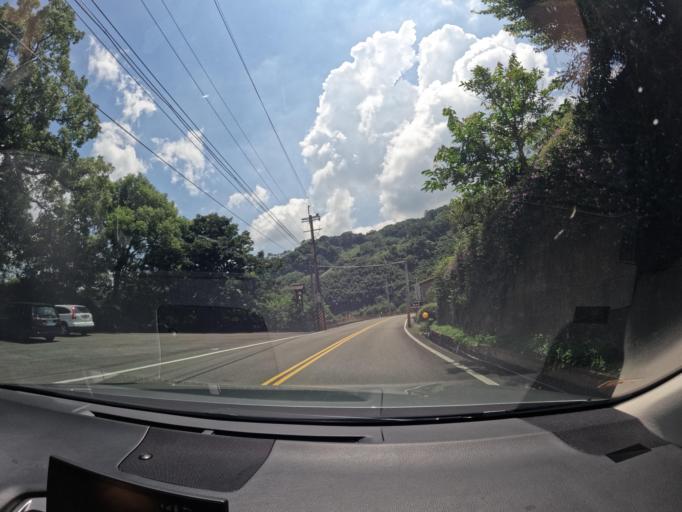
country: TW
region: Taiwan
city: Fengyuan
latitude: 24.3839
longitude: 120.8264
